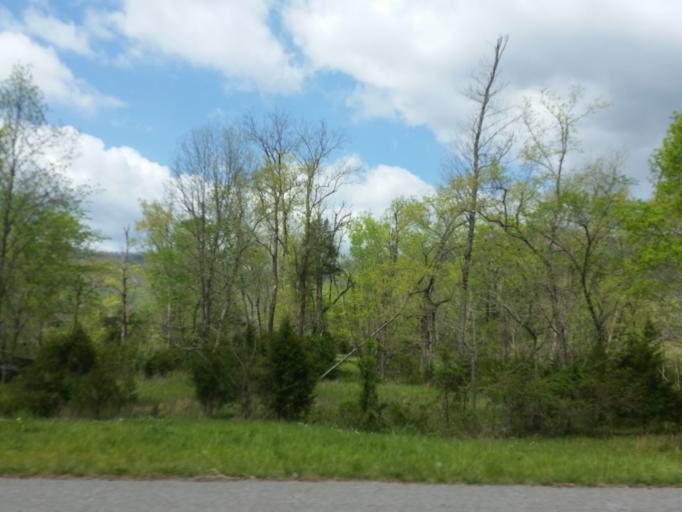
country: US
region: Tennessee
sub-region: Campbell County
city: Fincastle
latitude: 36.4455
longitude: -83.9620
